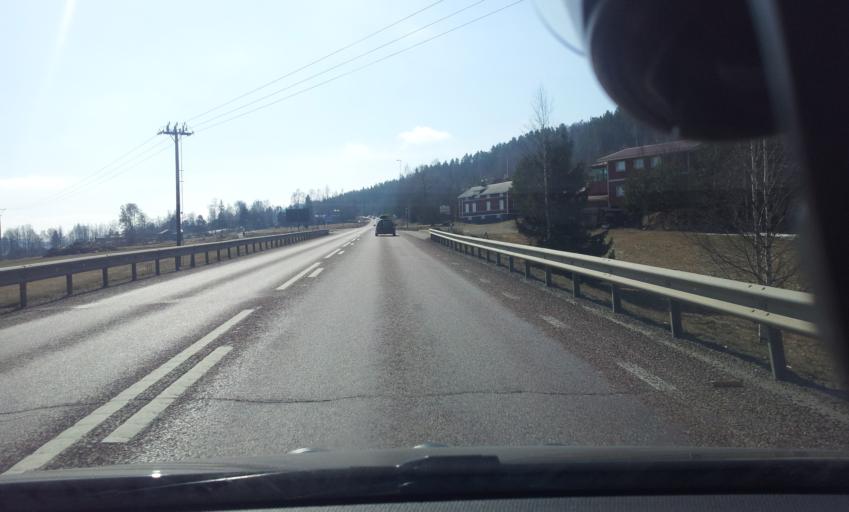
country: SE
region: Gaevleborg
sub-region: Ljusdals Kommun
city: Jaervsoe
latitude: 61.7492
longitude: 16.1599
